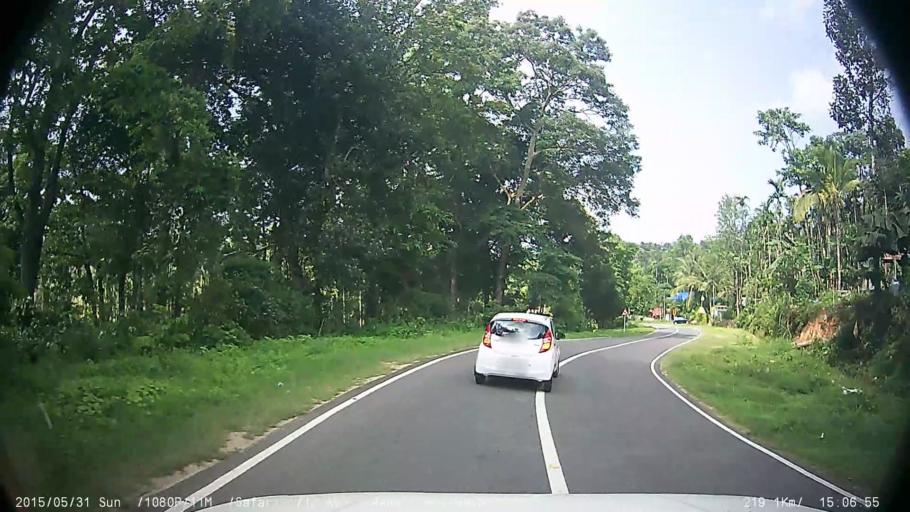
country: IN
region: Kerala
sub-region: Wayanad
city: Kalpetta
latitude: 11.6445
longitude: 76.2148
